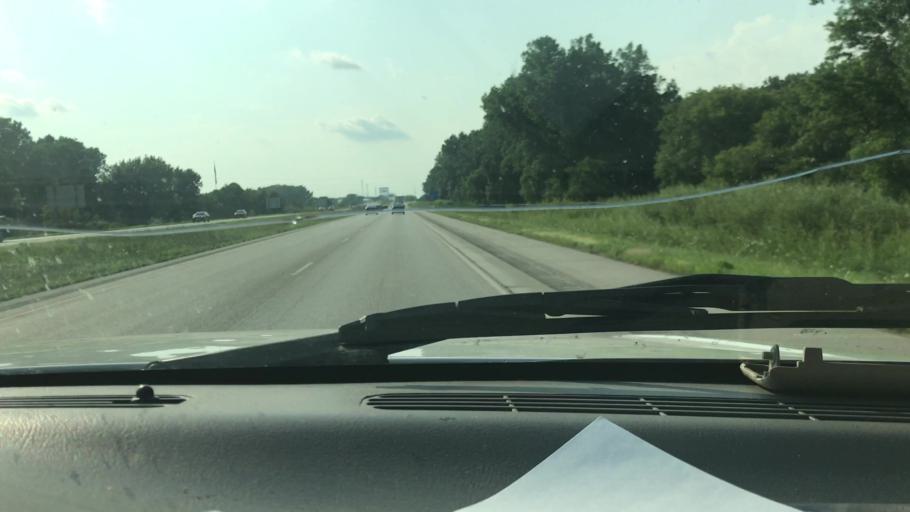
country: US
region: Wisconsin
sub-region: Brown County
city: Green Bay
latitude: 44.5221
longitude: -87.9744
